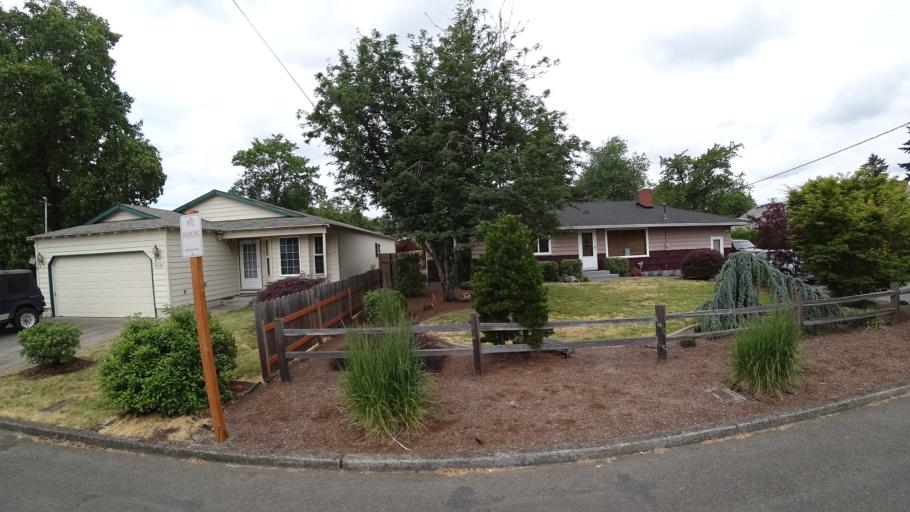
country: US
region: Oregon
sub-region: Multnomah County
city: Lents
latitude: 45.4858
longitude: -122.5569
